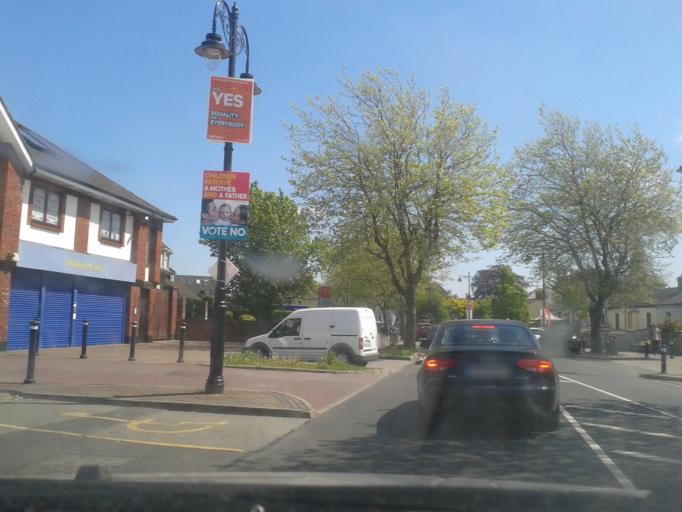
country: IE
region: Leinster
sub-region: Fingal County
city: Blanchardstown
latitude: 53.3867
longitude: -6.3770
